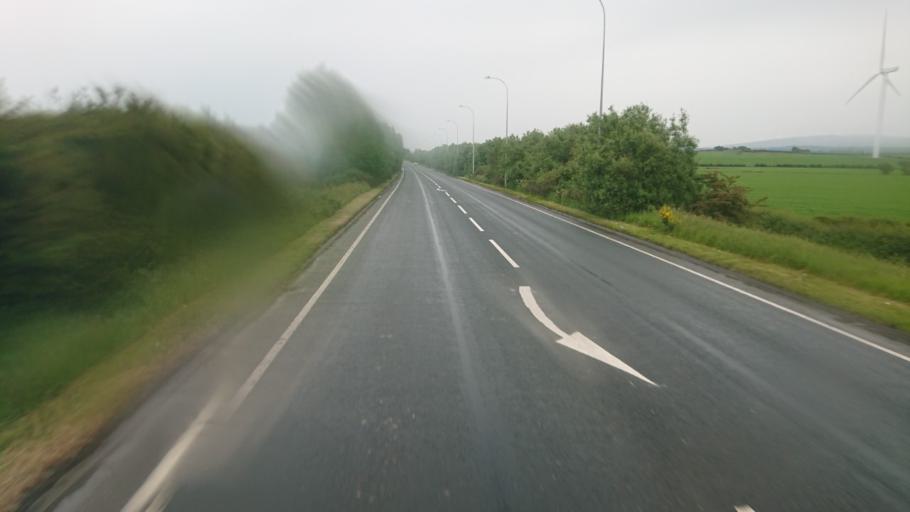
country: GB
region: England
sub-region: Lancashire
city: Morecambe
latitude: 54.0349
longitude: -2.8749
